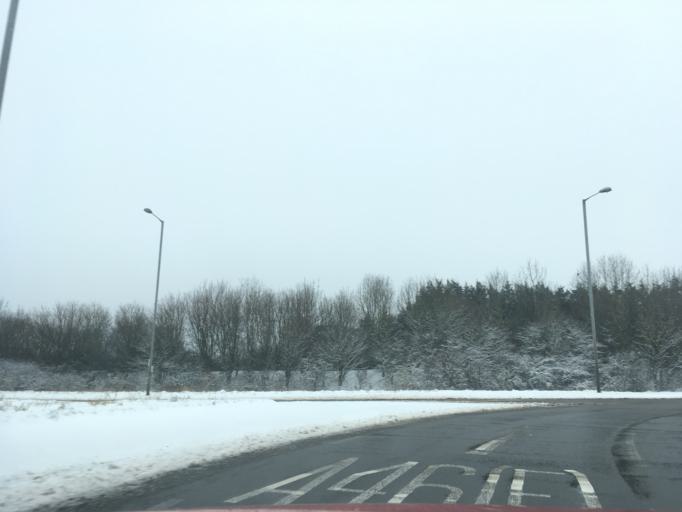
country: GB
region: England
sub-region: Warwickshire
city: Alcester
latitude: 52.2058
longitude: -1.8760
